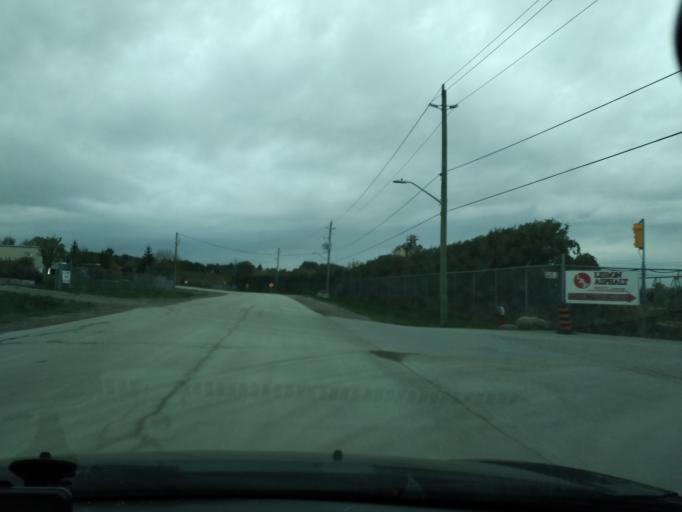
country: CA
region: Ontario
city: Bradford West Gwillimbury
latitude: 44.1395
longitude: -79.5560
